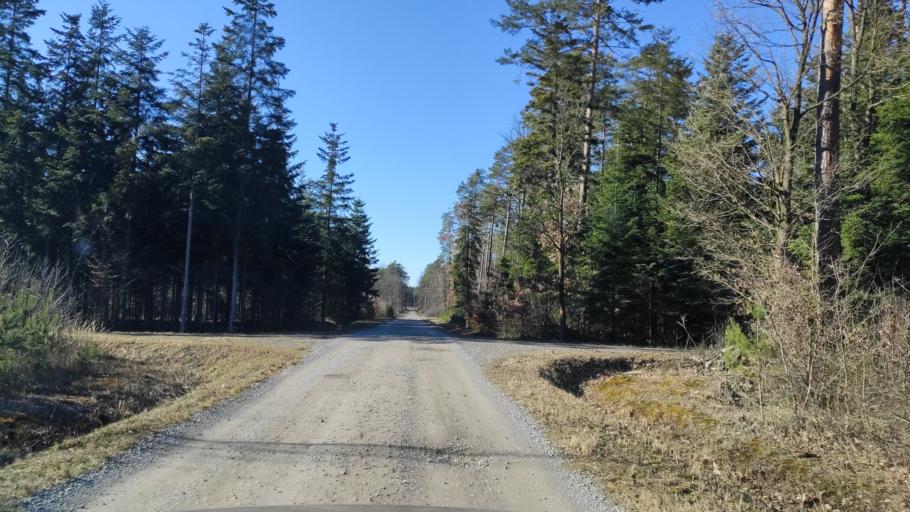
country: PL
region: Masovian Voivodeship
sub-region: Powiat radomski
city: Jedlnia-Letnisko
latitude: 51.4704
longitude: 21.3047
